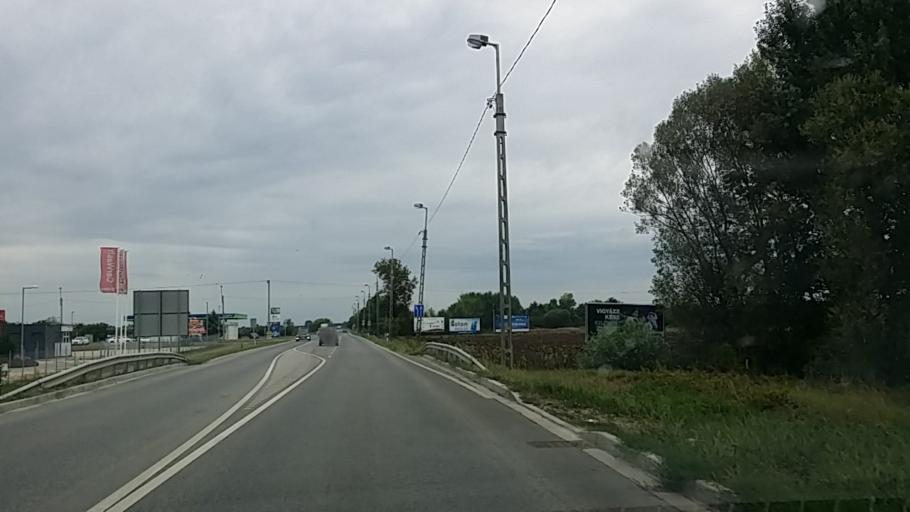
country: HU
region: Gyor-Moson-Sopron
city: Kapuvar
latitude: 47.5903
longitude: 17.0119
